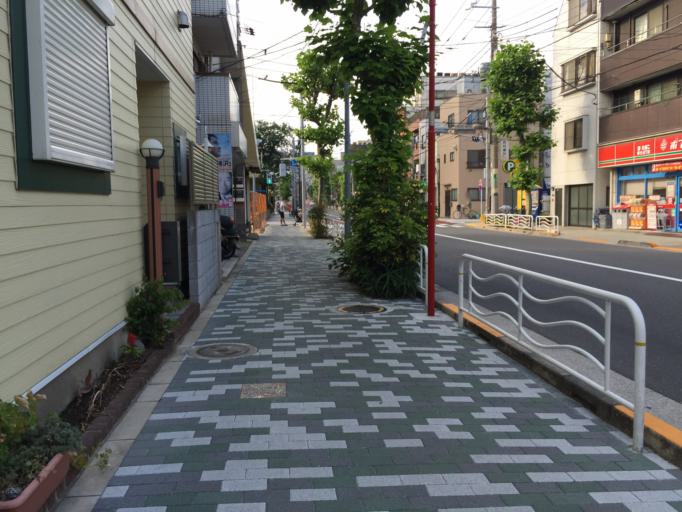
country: JP
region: Tokyo
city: Urayasu
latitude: 35.6658
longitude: 139.8006
